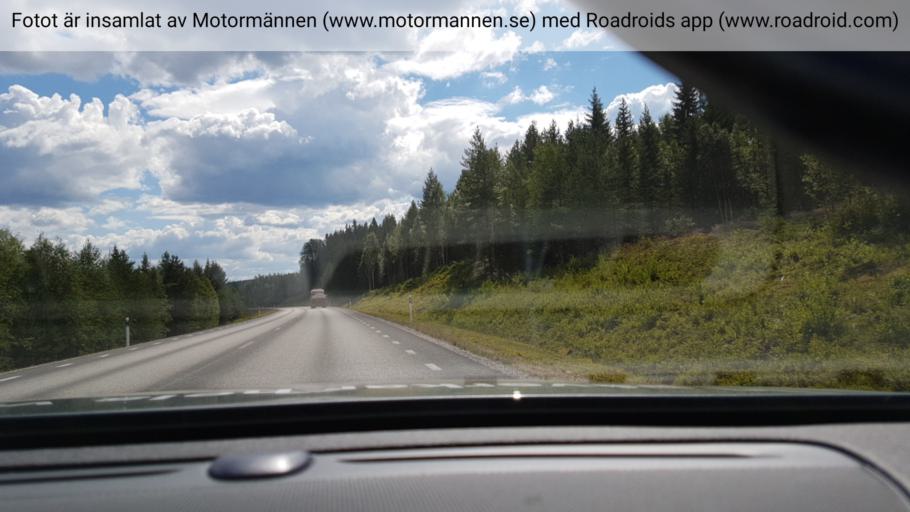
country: SE
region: Dalarna
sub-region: Faluns Kommun
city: Bjursas
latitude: 60.7516
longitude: 15.3492
